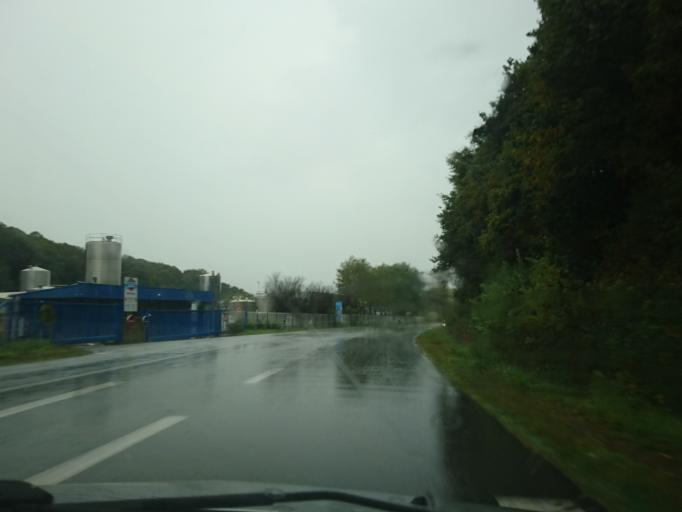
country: FR
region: Brittany
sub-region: Departement du Finistere
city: Plouvien
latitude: 48.5406
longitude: -4.4888
